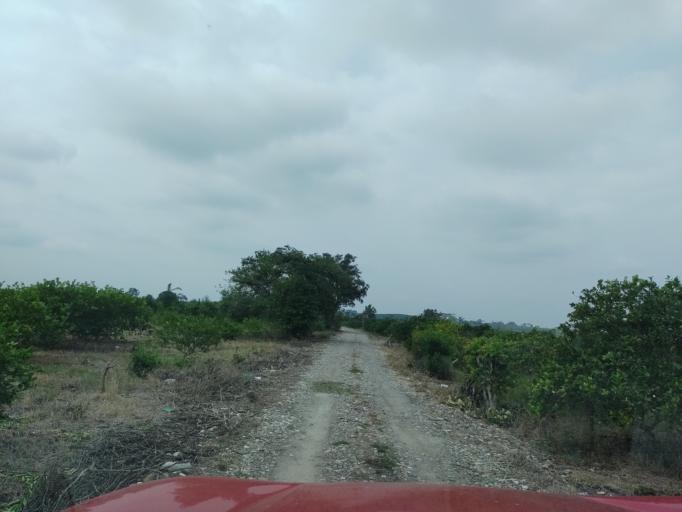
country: MX
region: Veracruz
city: Agua Dulce
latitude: 20.3414
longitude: -97.2959
